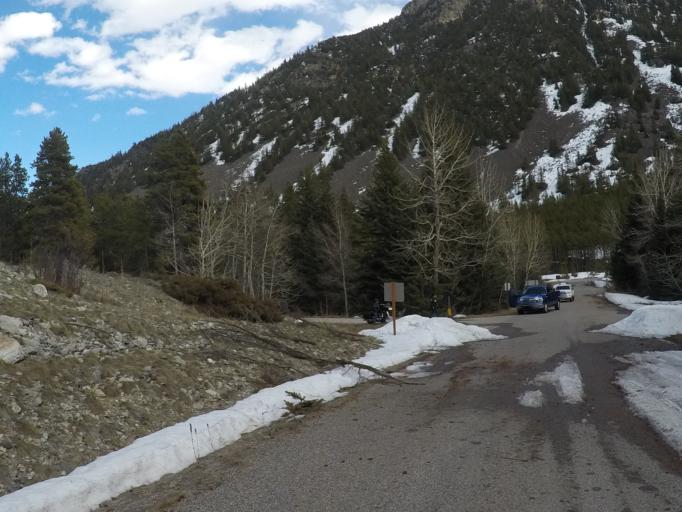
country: US
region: Montana
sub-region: Carbon County
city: Red Lodge
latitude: 45.0829
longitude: -109.3774
